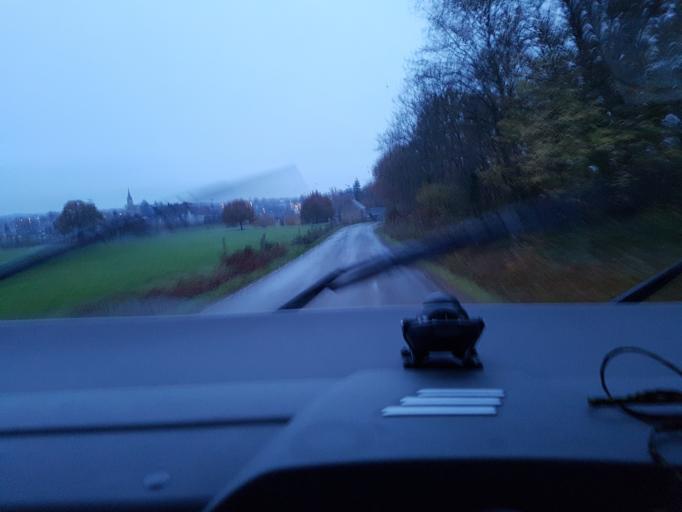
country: FR
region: Brittany
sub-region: Departement d'Ille-et-Vilaine
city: Livre-sur-Changeon
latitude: 48.1820
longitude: -1.2942
